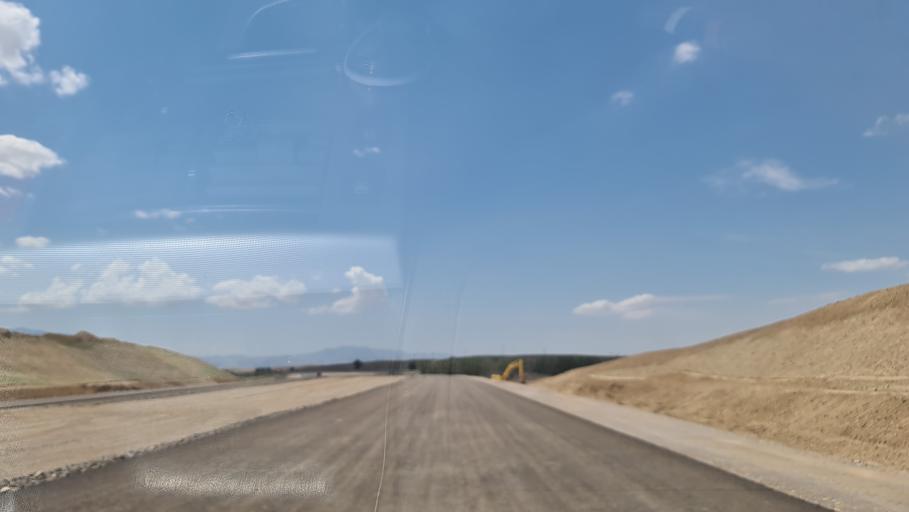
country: KG
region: Chuy
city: Bystrovka
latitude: 43.3251
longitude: 75.8216
